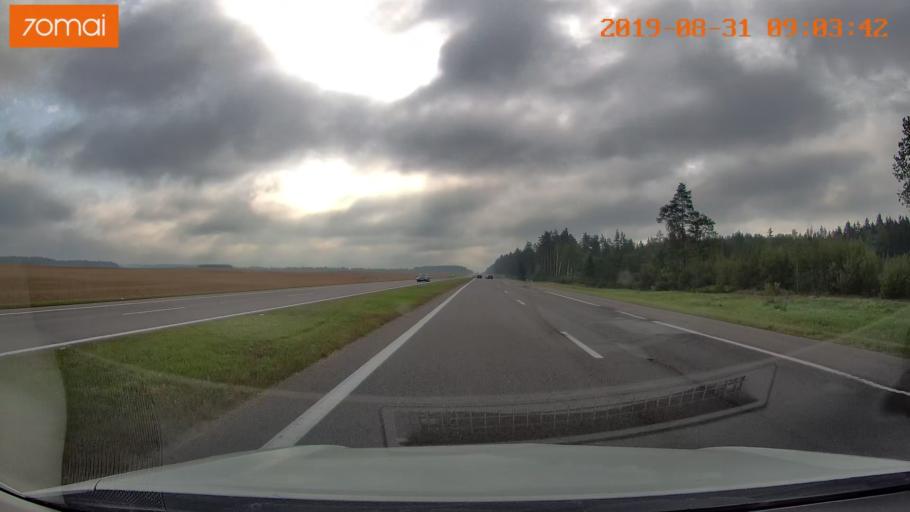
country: BY
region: Minsk
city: Chervyen'
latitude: 53.7381
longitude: 28.3245
